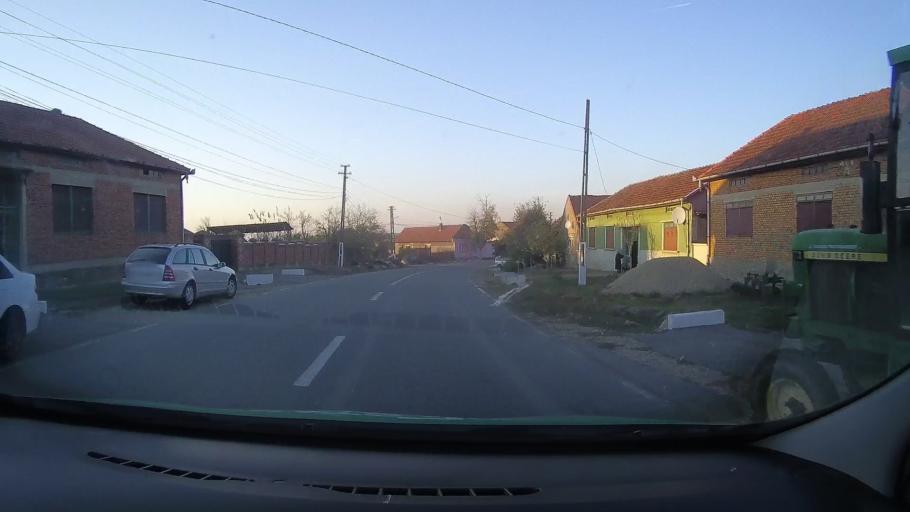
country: RO
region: Timis
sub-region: Comuna Traian Vuia
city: Traian Vuia
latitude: 45.8008
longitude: 22.0241
